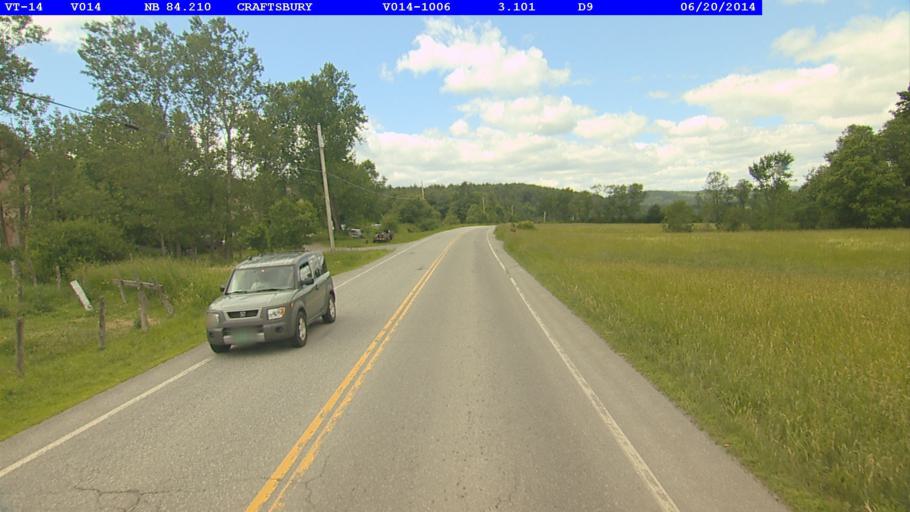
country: US
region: Vermont
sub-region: Caledonia County
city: Hardwick
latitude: 44.6365
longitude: -72.3975
